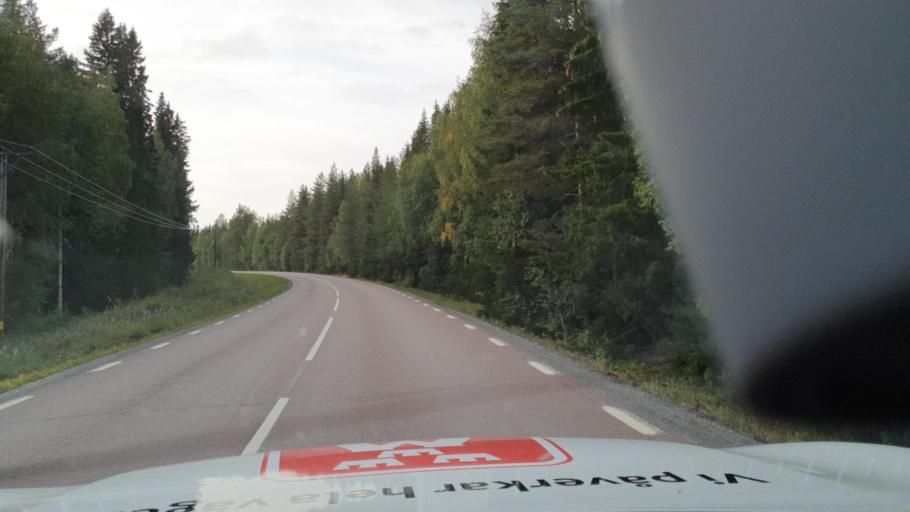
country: SE
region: Jaemtland
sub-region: Stroemsunds Kommun
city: Stroemsund
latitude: 63.8159
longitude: 15.6429
